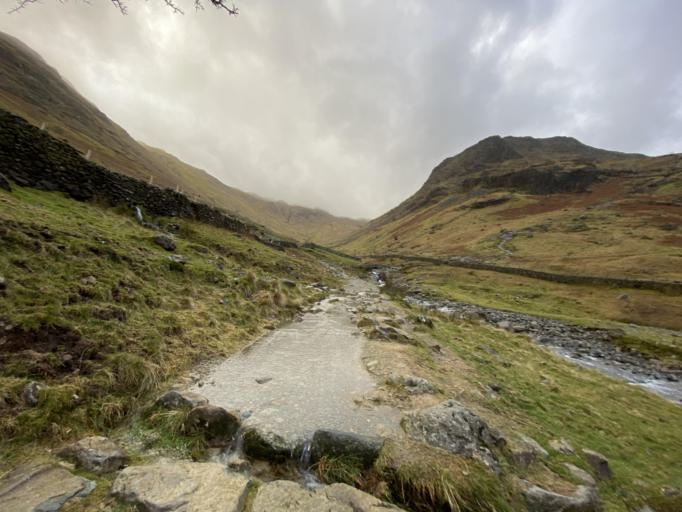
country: GB
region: England
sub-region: Cumbria
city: Keswick
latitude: 54.4886
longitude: -3.1827
